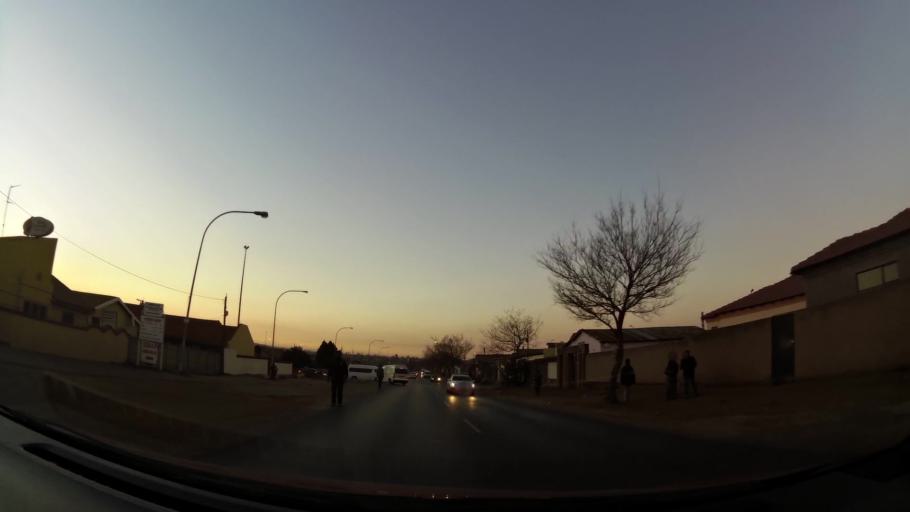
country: ZA
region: Gauteng
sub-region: City of Johannesburg Metropolitan Municipality
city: Soweto
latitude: -26.2335
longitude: 27.8259
